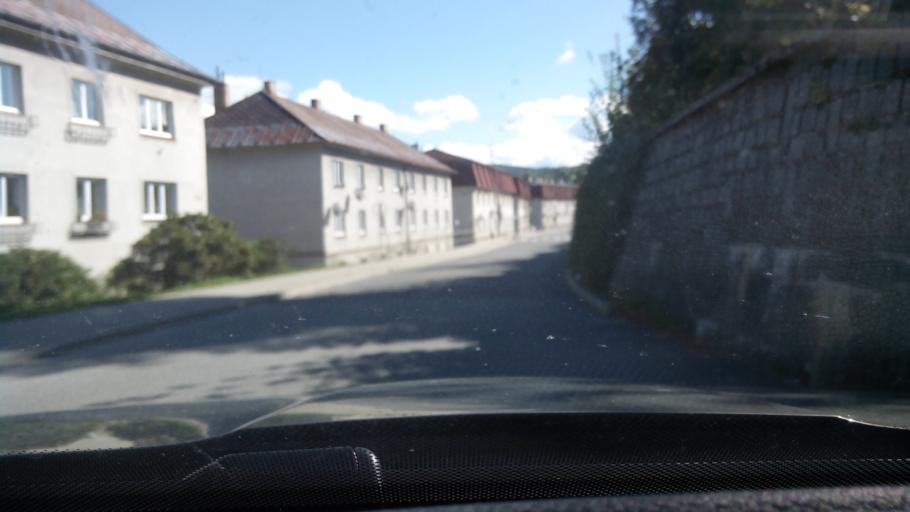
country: CZ
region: Jihocesky
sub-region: Okres Prachatice
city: Vimperk
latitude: 49.0575
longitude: 13.7780
